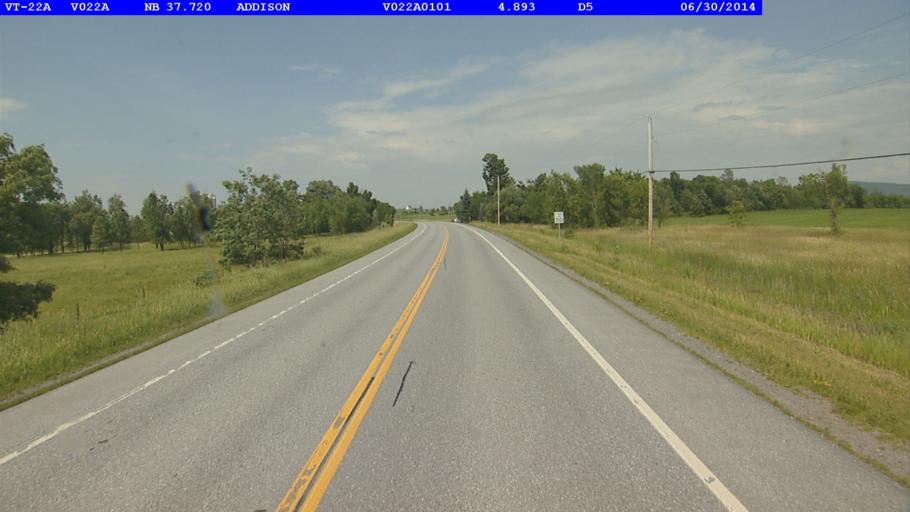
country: US
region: Vermont
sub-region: Addison County
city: Vergennes
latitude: 44.0995
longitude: -73.2979
